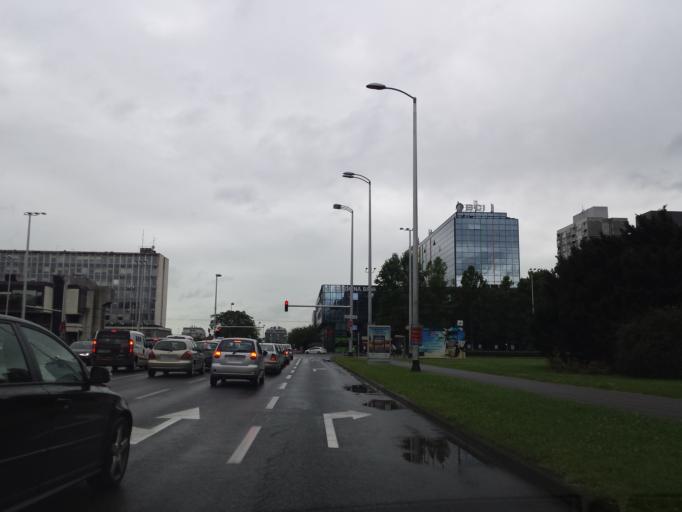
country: HR
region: Grad Zagreb
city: Zagreb - Centar
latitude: 45.8009
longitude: 15.9744
